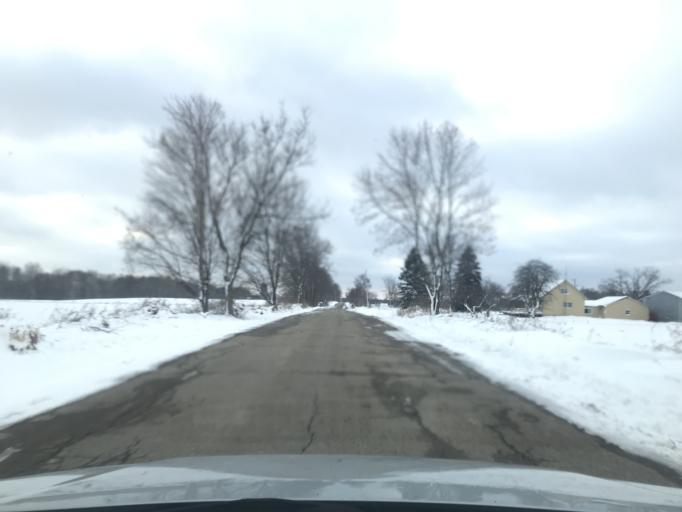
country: US
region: Wisconsin
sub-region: Oconto County
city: Oconto
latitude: 44.9245
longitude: -87.9971
